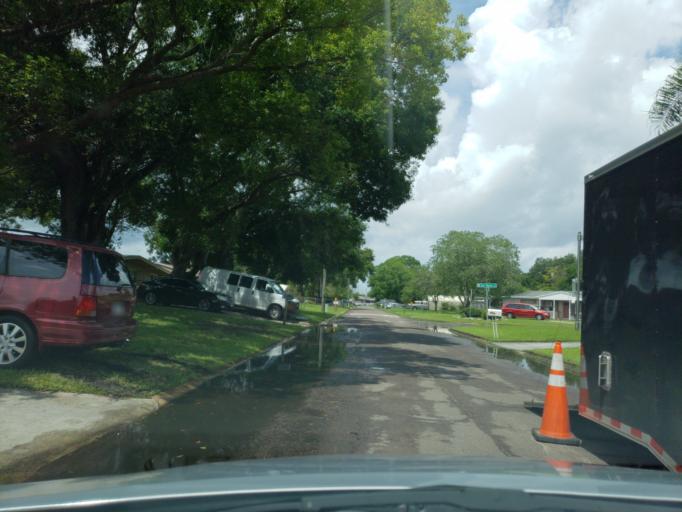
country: US
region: Florida
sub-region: Hillsborough County
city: Progress Village
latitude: 27.9235
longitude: -82.3457
